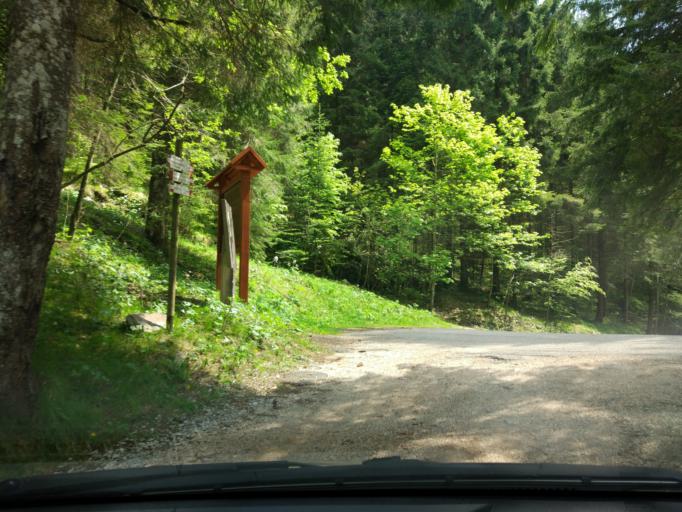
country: IT
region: Veneto
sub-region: Provincia di Verona
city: Selva di Progno
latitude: 45.6846
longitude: 11.1191
